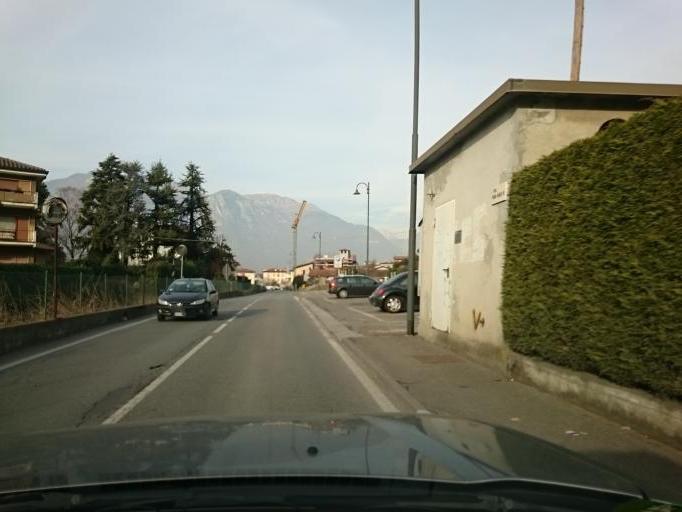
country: IT
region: Lombardy
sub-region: Provincia di Brescia
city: Pisogne
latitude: 45.8002
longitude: 10.1060
